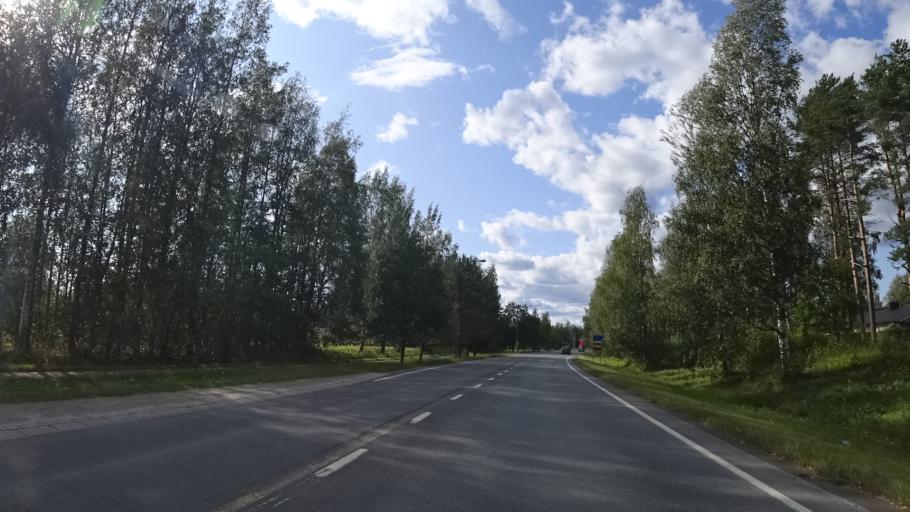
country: FI
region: North Karelia
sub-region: Keski-Karjala
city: Tohmajaervi
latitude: 62.2238
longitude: 30.3403
